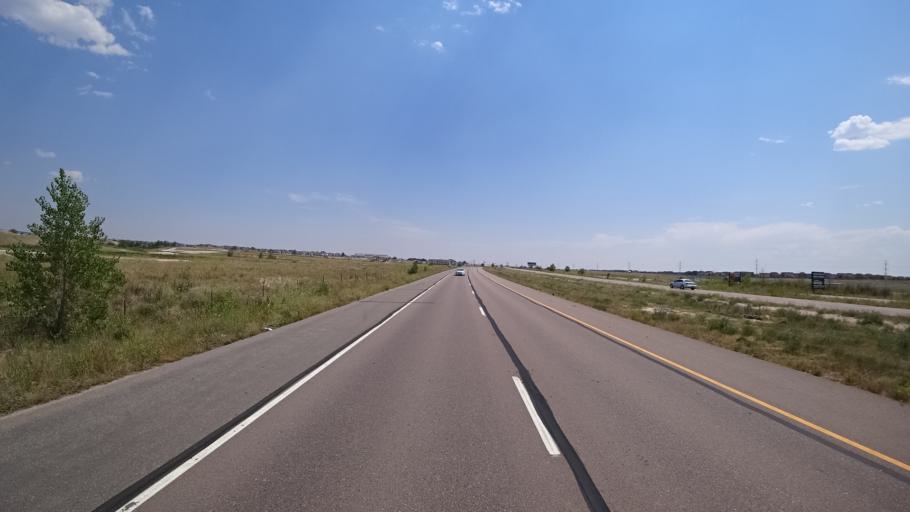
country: US
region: Colorado
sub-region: El Paso County
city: Black Forest
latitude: 38.9414
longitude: -104.6856
